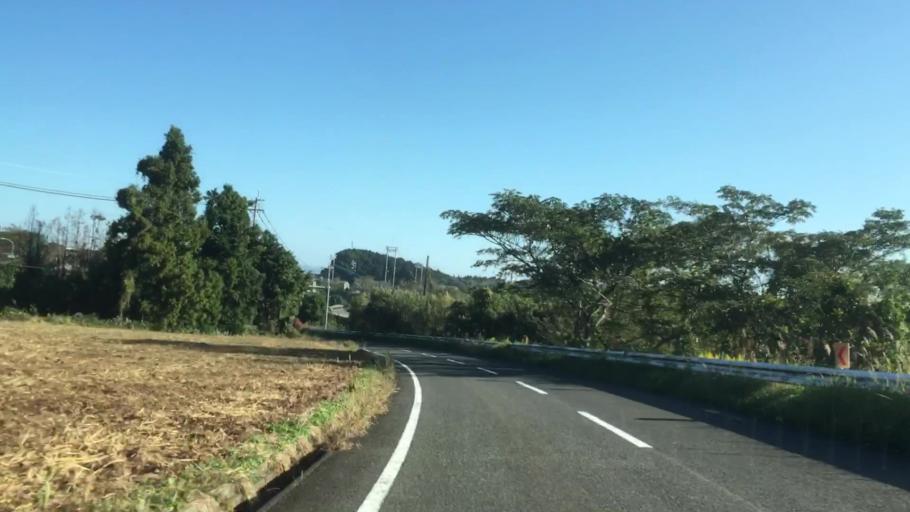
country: JP
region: Nagasaki
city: Sasebo
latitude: 33.0403
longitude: 129.6953
